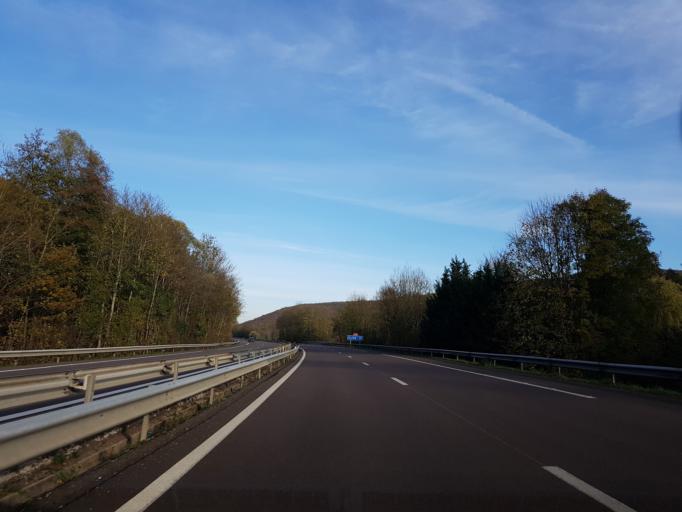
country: FR
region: Bourgogne
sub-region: Departement de la Cote-d'Or
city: Fleurey-sur-Ouche
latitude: 47.2976
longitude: 4.8112
